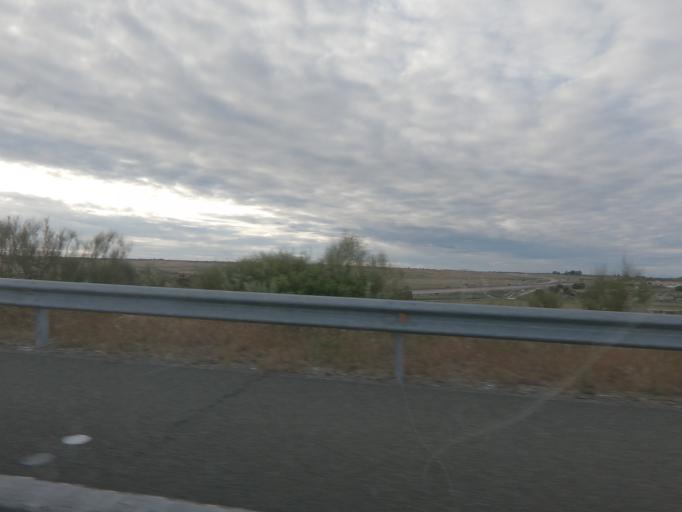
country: ES
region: Extremadura
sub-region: Provincia de Caceres
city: Casar de Caceres
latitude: 39.5144
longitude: -6.4272
